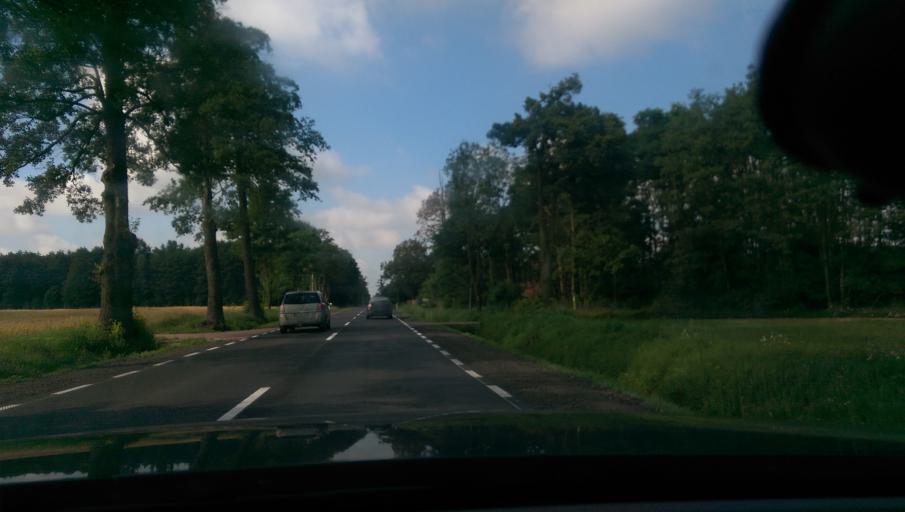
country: PL
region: Masovian Voivodeship
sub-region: Powiat ciechanowski
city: Ojrzen
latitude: 52.7293
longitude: 20.5129
